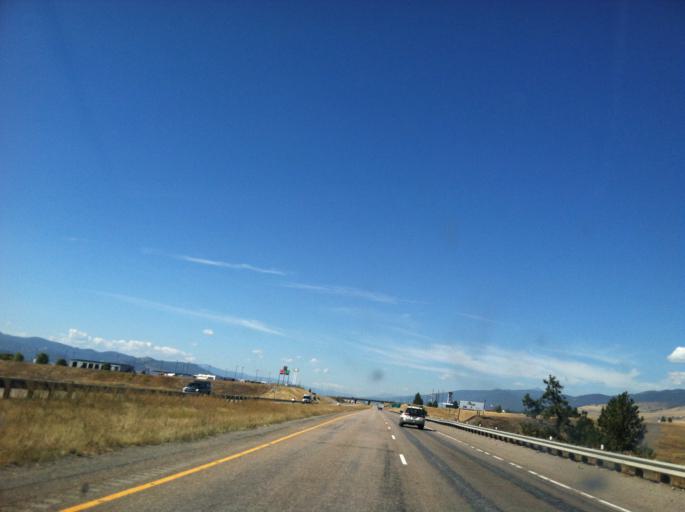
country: US
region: Montana
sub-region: Missoula County
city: Orchard Homes
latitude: 46.9449
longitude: -114.1199
